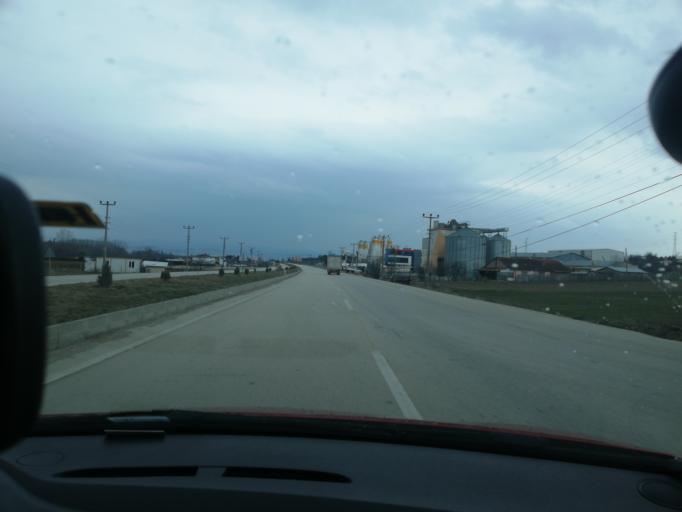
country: TR
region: Kastamonu
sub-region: Cide
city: Kastamonu
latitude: 41.4778
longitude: 33.7691
